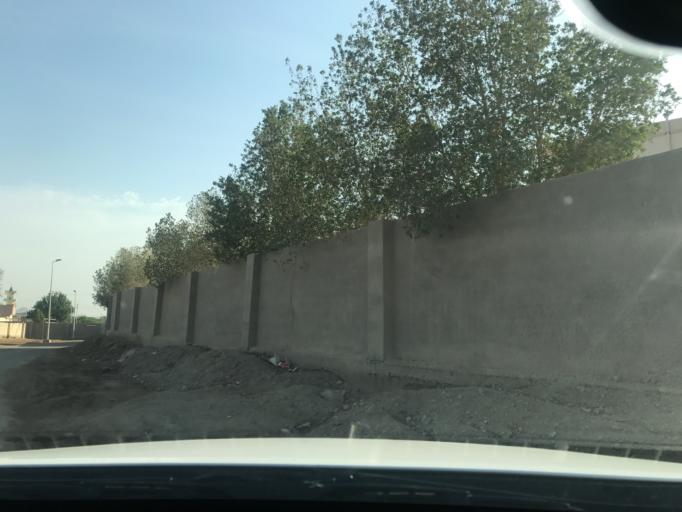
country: SA
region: Makkah
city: Al Jumum
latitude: 21.4534
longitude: 39.5357
